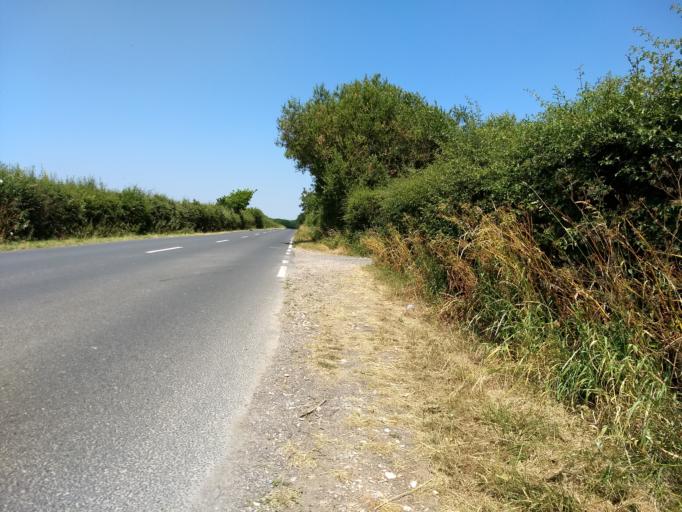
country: GB
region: England
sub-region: Isle of Wight
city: Northwood
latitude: 50.7053
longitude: -1.3467
